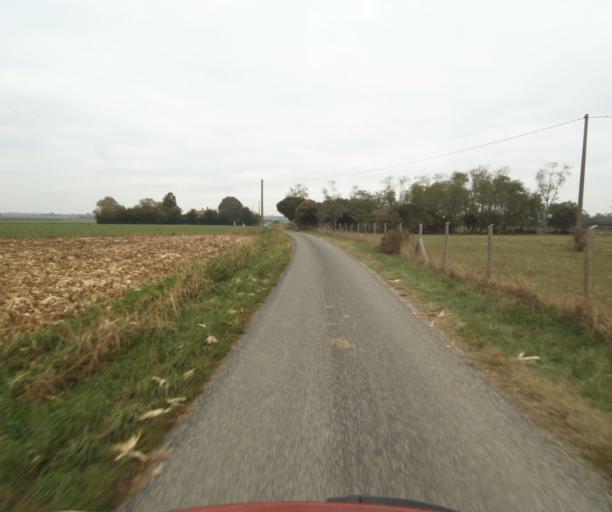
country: FR
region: Midi-Pyrenees
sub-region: Departement du Tarn-et-Garonne
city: Verdun-sur-Garonne
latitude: 43.8130
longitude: 1.2328
